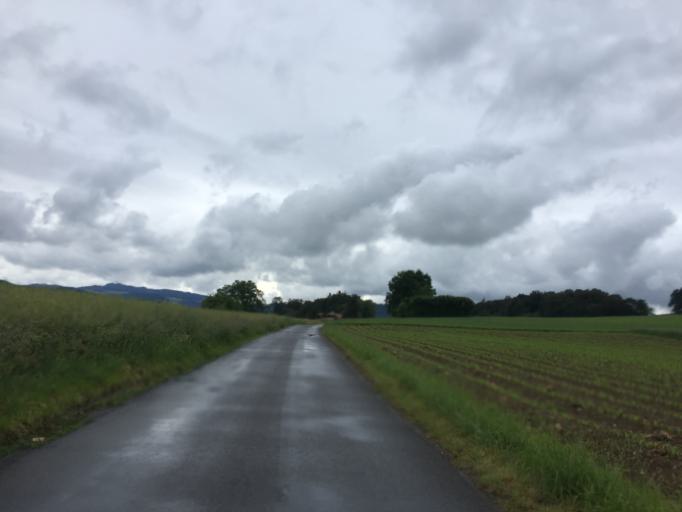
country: CH
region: Bern
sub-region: Bern-Mittelland District
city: Taegertschi
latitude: 46.8900
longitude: 7.5784
